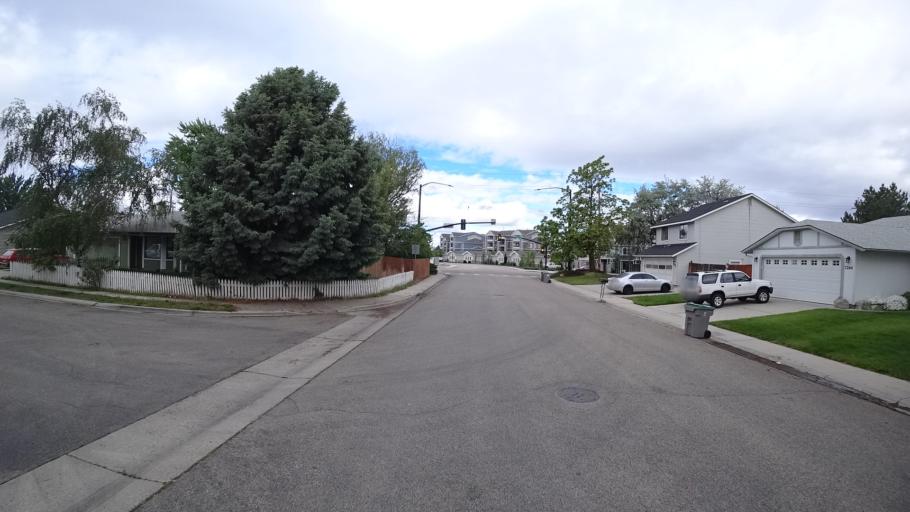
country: US
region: Idaho
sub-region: Ada County
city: Garden City
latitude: 43.6716
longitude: -116.2786
